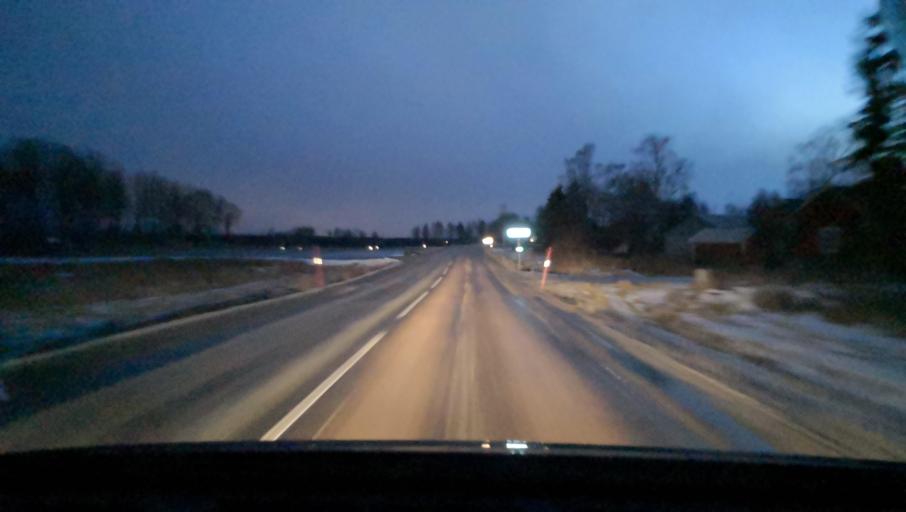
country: SE
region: Vaestmanland
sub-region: Vasteras
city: Skultuna
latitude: 59.7667
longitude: 16.4617
